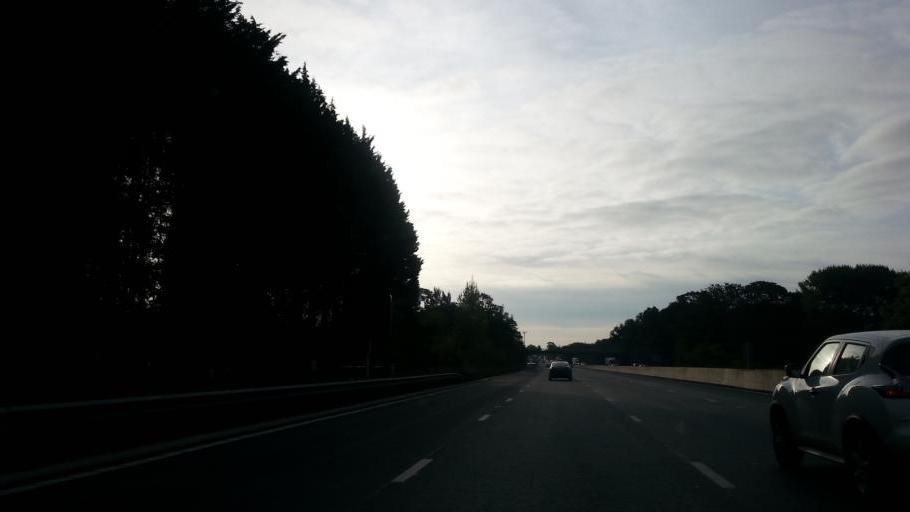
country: GB
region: England
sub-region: Northamptonshire
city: Long Buckby
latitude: 52.2547
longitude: -1.0772
